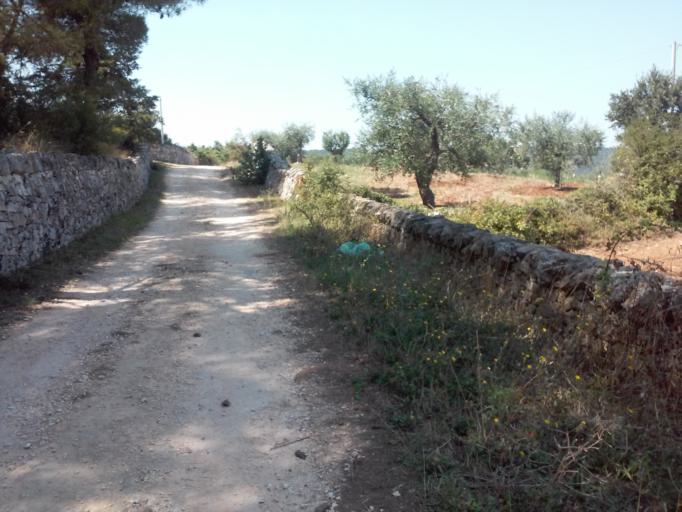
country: IT
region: Apulia
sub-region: Provincia di Bari
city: Alberobello
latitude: 40.8046
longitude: 17.2049
